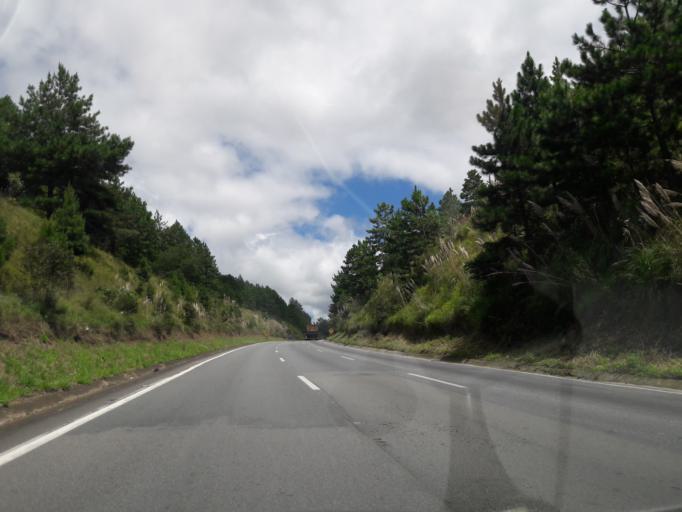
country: BR
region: Parana
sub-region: Campina Grande Do Sul
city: Campina Grande do Sul
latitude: -25.1044
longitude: -48.8376
